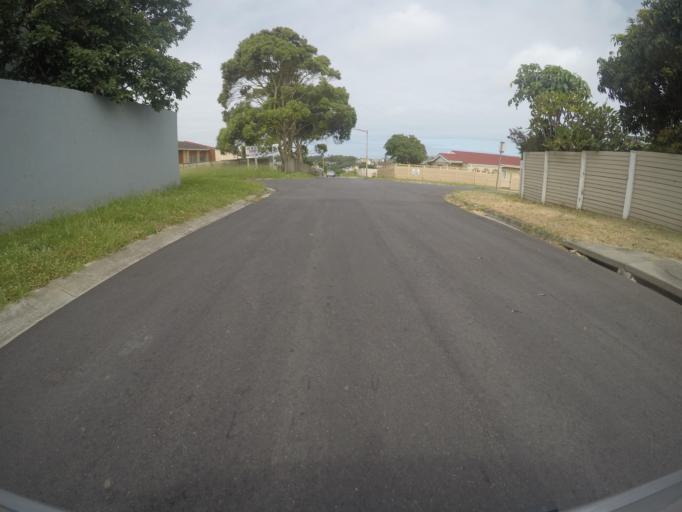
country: ZA
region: Eastern Cape
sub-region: Buffalo City Metropolitan Municipality
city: East London
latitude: -33.0002
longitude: 27.8788
